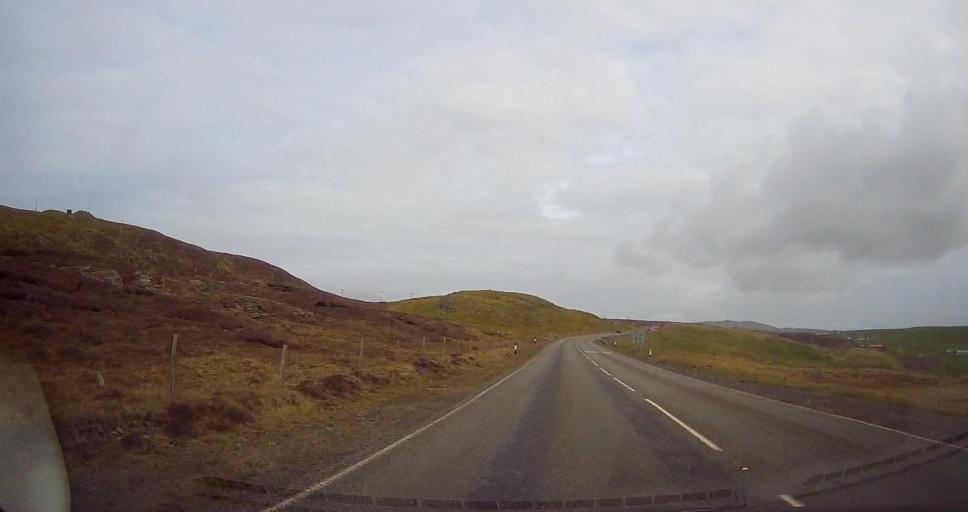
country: GB
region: Scotland
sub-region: Shetland Islands
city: Lerwick
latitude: 60.1068
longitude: -1.2192
